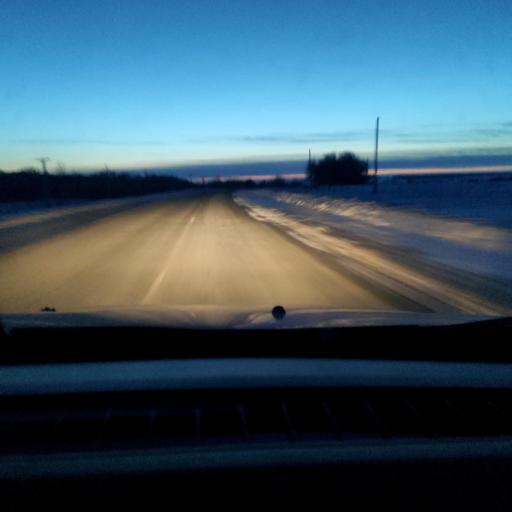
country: RU
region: Samara
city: Kinel'
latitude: 53.2954
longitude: 50.7358
